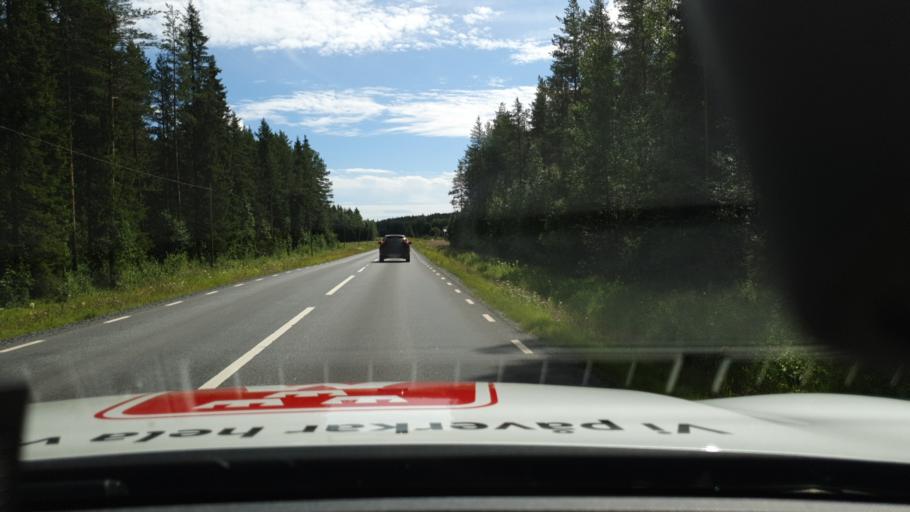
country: SE
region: Norrbotten
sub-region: Lulea Kommun
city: Ranea
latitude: 65.7878
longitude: 22.1555
